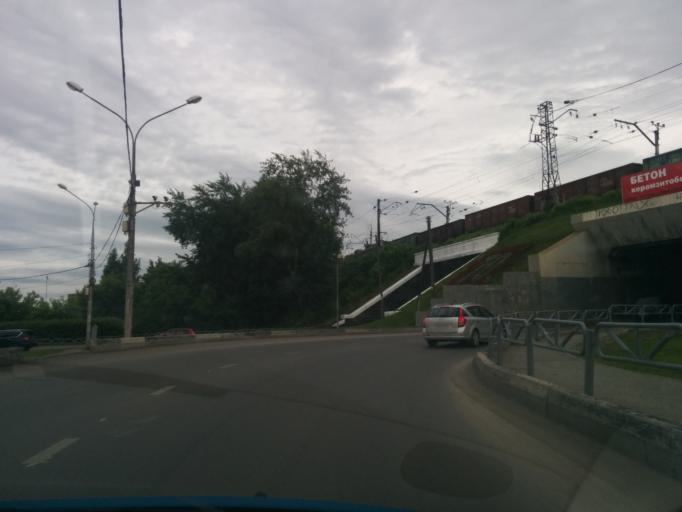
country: RU
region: Perm
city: Perm
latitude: 58.0036
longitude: 56.1942
